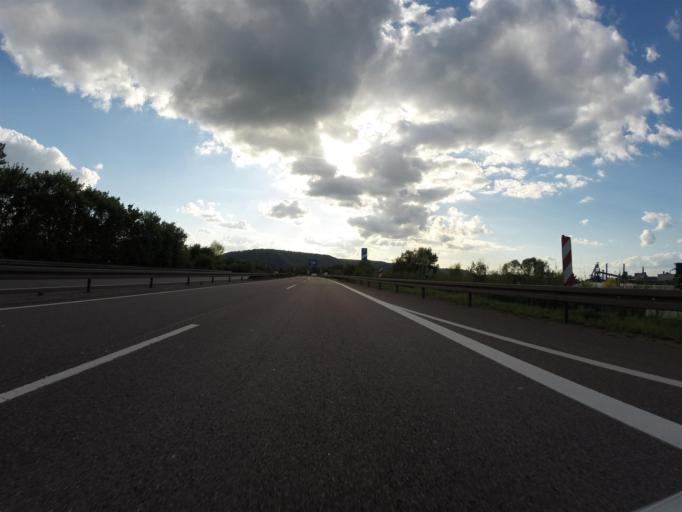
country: DE
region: Saarland
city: Dillingen
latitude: 49.3422
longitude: 6.7455
